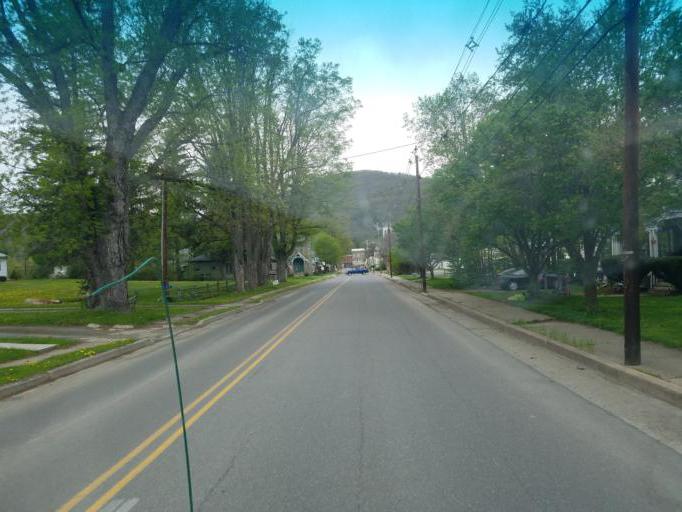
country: US
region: Pennsylvania
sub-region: Tioga County
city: Westfield
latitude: 41.9164
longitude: -77.5376
